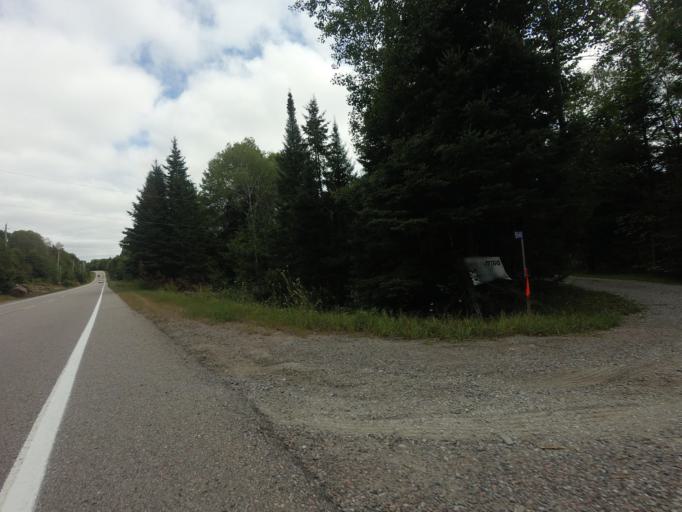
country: CA
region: Ontario
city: Omemee
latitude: 44.8987
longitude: -78.4475
